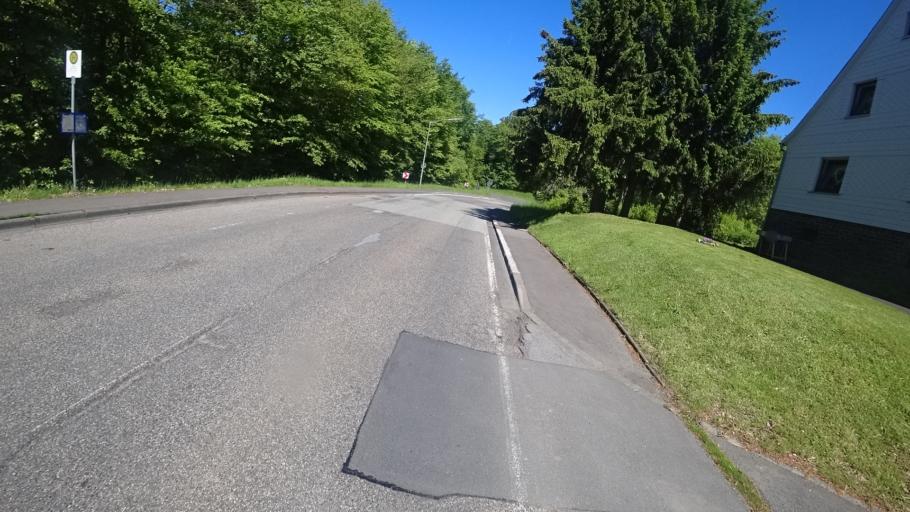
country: DE
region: Rheinland-Pfalz
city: Kausen
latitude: 50.7431
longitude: 7.8727
